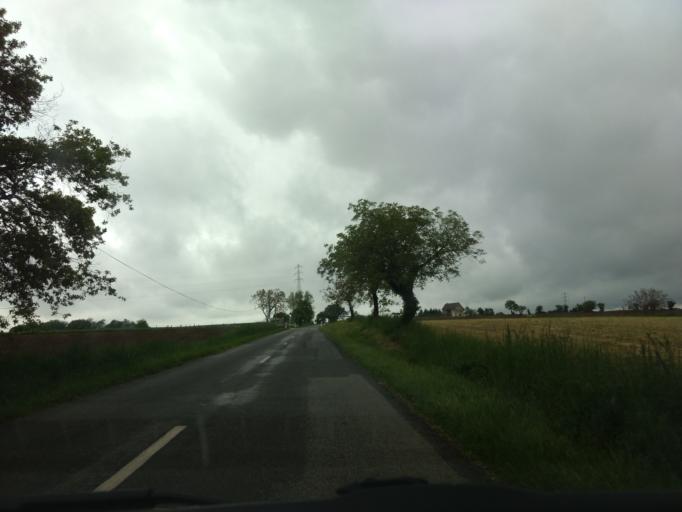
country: FR
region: Midi-Pyrenees
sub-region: Departement de l'Aveyron
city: Montbazens
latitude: 44.5014
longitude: 2.1985
